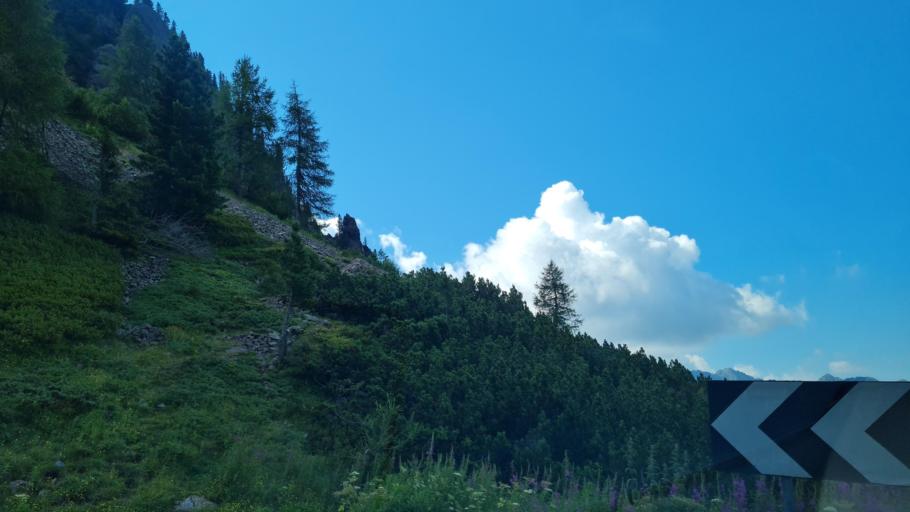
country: IT
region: Trentino-Alto Adige
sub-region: Provincia di Trento
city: Torcegno
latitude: 46.1682
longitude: 11.4425
